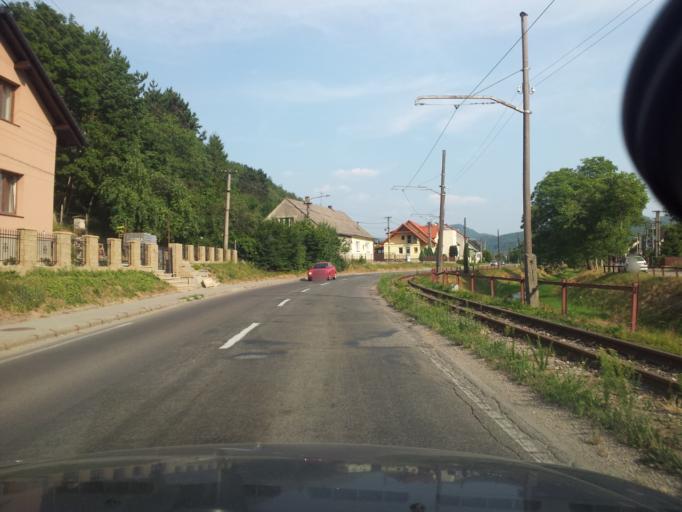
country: SK
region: Trenciansky
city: Nova Dubnica
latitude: 48.9313
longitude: 18.1272
